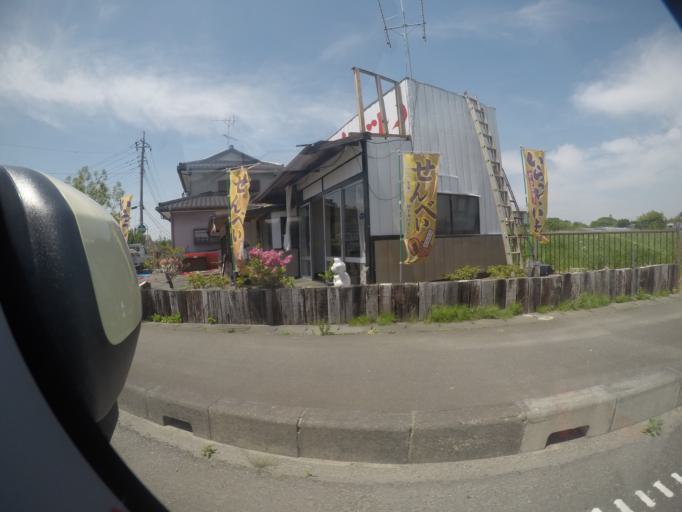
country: JP
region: Ibaraki
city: Makabe
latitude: 36.2493
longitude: 140.0711
